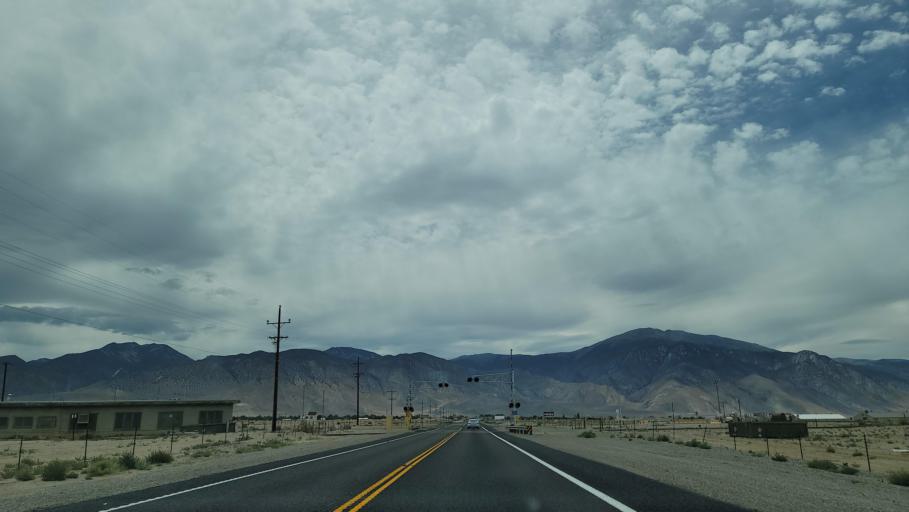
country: US
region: Nevada
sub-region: Mineral County
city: Hawthorne
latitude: 38.5246
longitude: -118.5966
